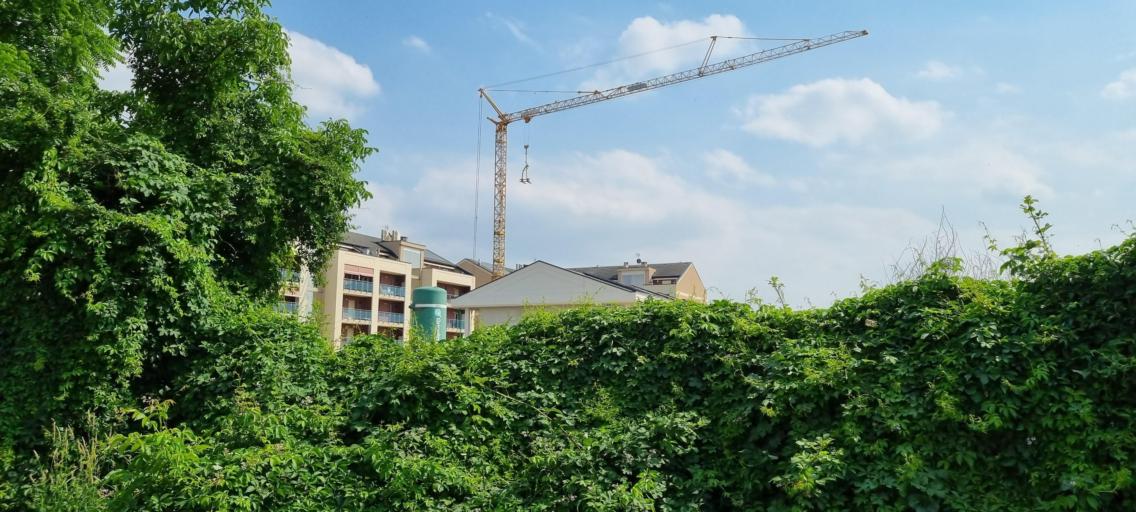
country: IT
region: Piedmont
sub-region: Provincia di Torino
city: Carignano
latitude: 44.9091
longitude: 7.6670
